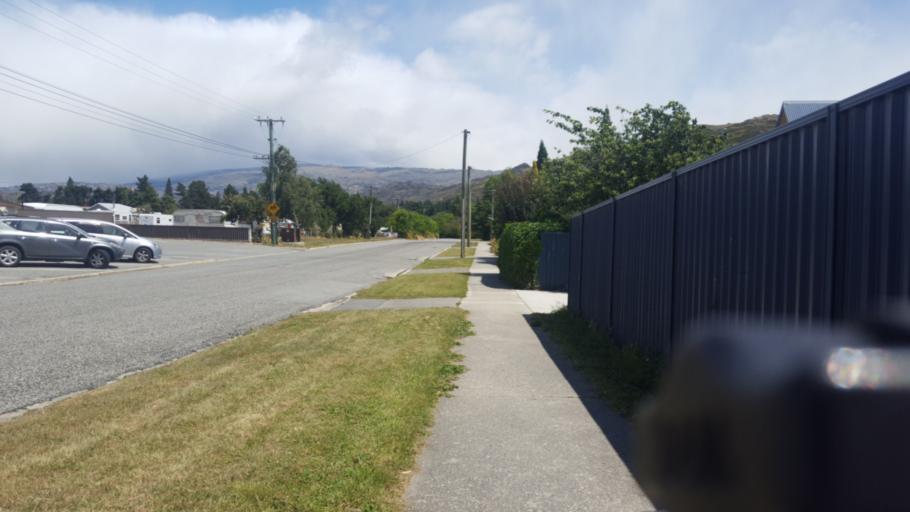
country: NZ
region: Otago
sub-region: Queenstown-Lakes District
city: Wanaka
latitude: -45.1907
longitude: 169.3210
